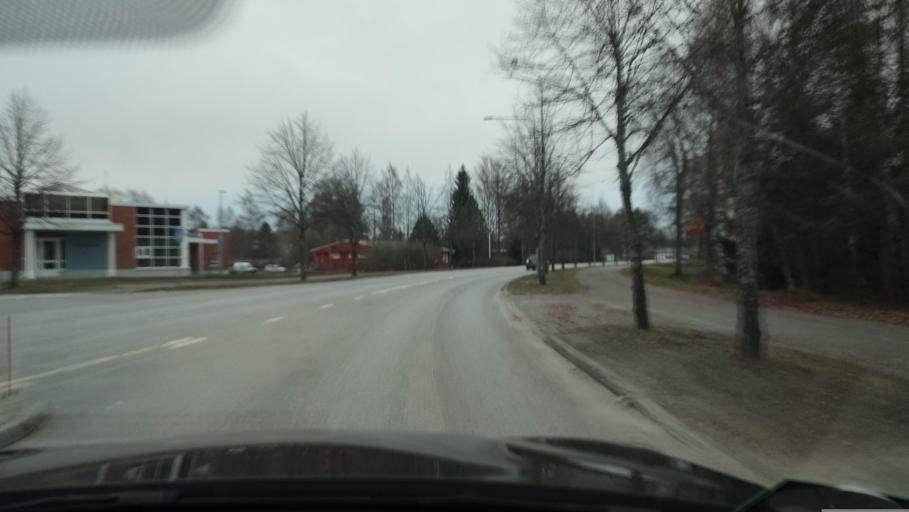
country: FI
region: Southern Ostrobothnia
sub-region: Suupohja
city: Kauhajoki
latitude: 62.4201
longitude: 22.1764
